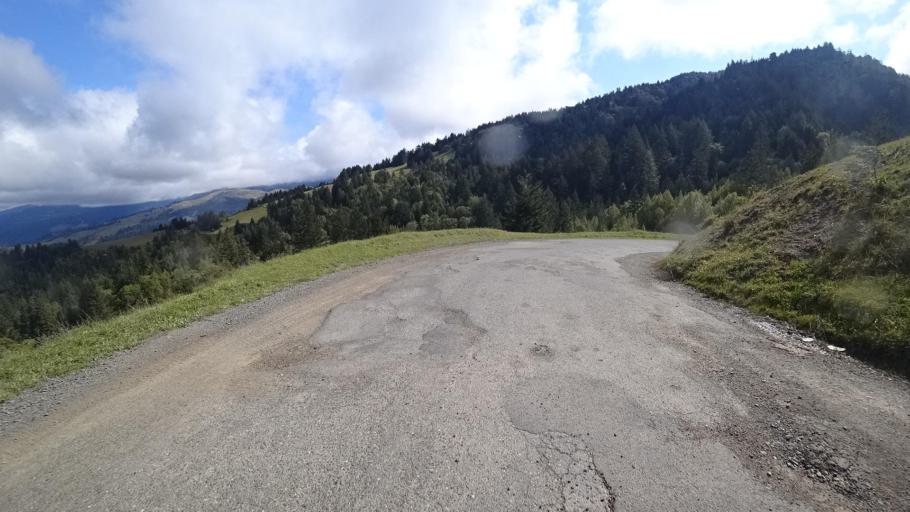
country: US
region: California
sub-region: Humboldt County
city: Redway
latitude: 40.1626
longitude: -123.5638
